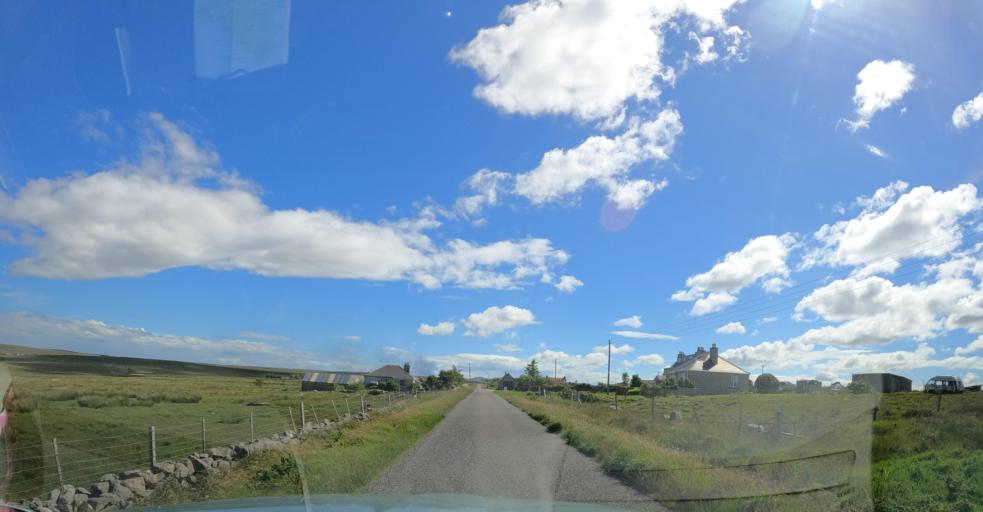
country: GB
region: Scotland
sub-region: Eilean Siar
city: Isle of Lewis
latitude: 58.3517
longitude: -6.5469
